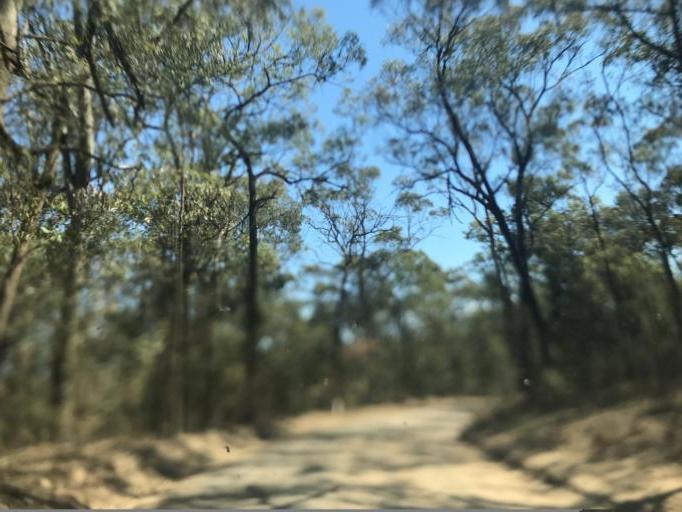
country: AU
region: New South Wales
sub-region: Hawkesbury
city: Pitt Town
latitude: -33.4643
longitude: 150.8436
